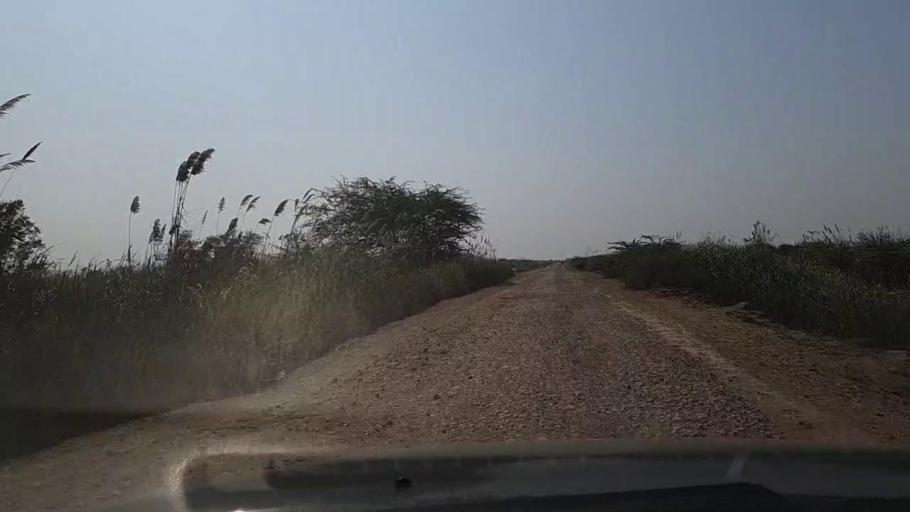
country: PK
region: Sindh
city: Mirpur Sakro
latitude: 24.3797
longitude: 67.6597
